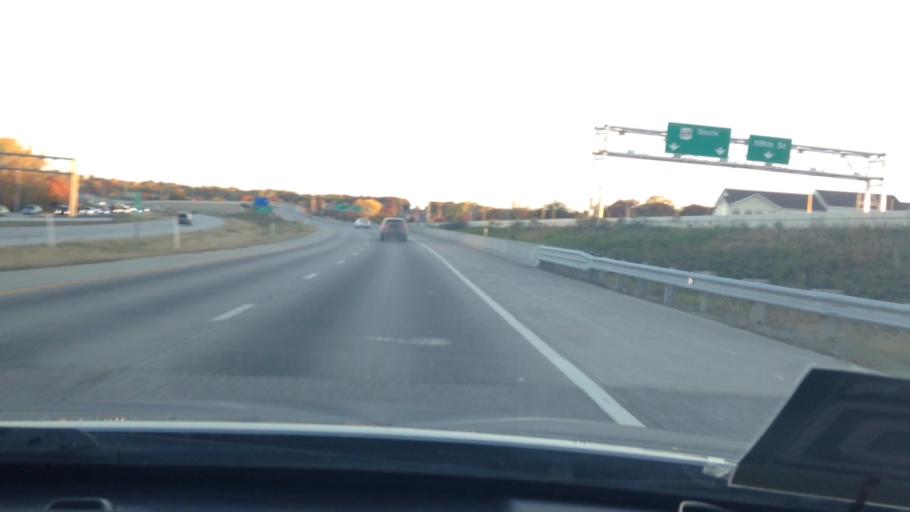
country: US
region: Kansas
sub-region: Johnson County
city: Lenexa
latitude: 38.9244
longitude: -94.7058
